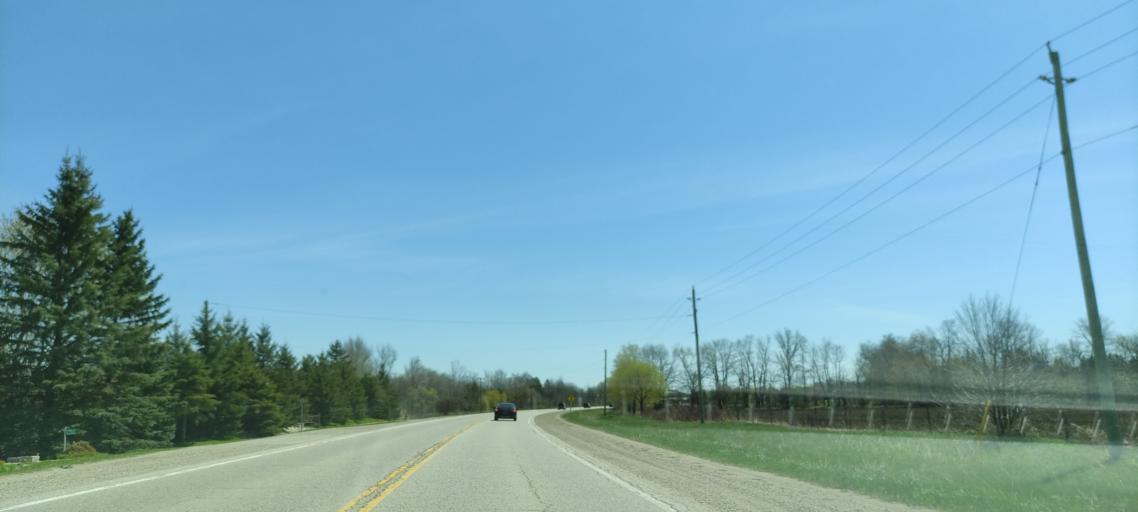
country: CA
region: Ontario
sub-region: Wellington County
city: Guelph
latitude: 43.5757
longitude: -80.3719
